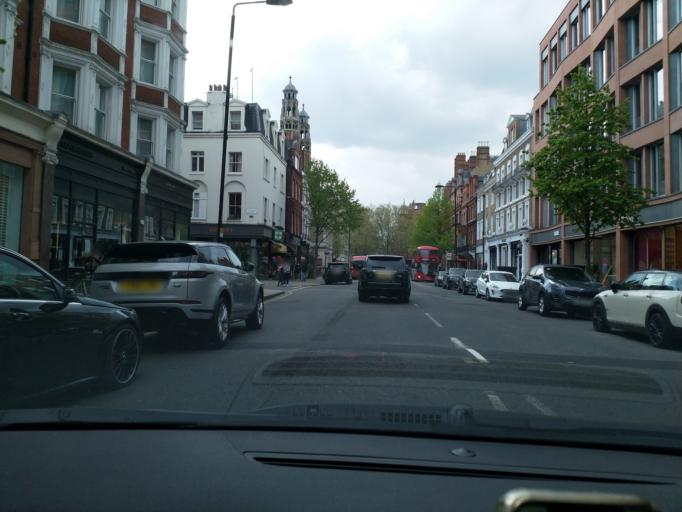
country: GB
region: England
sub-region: Greater London
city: Chelsea
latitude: 51.4938
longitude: -0.1580
